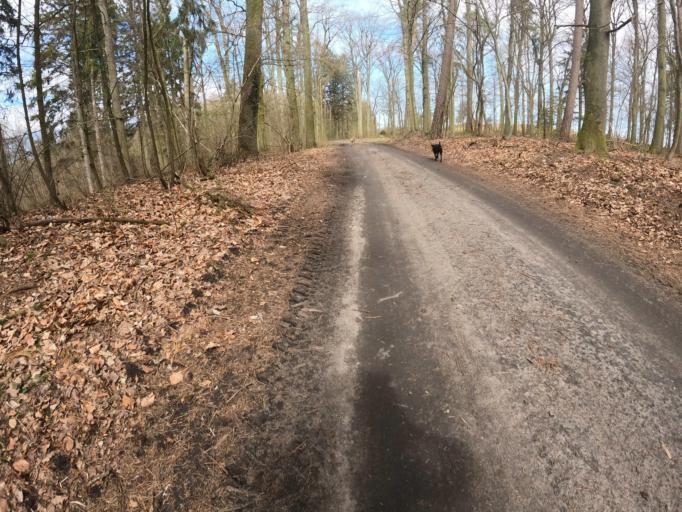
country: PL
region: West Pomeranian Voivodeship
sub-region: Powiat gryficki
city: Brojce
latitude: 53.9611
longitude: 15.3740
